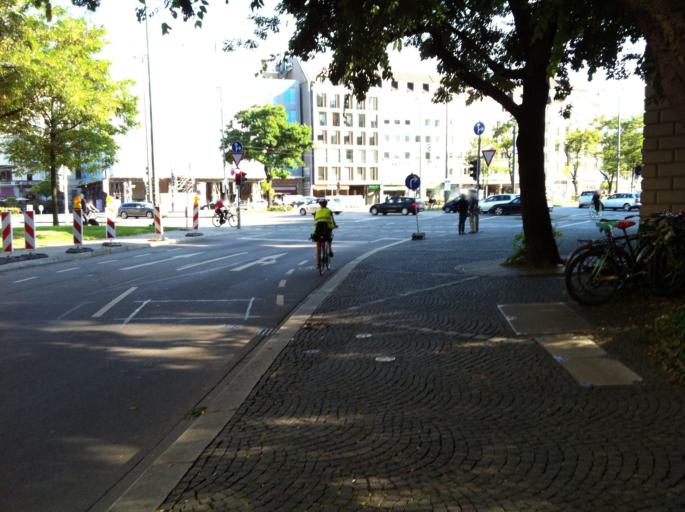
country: DE
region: Bavaria
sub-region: Upper Bavaria
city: Munich
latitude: 48.1410
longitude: 11.5665
